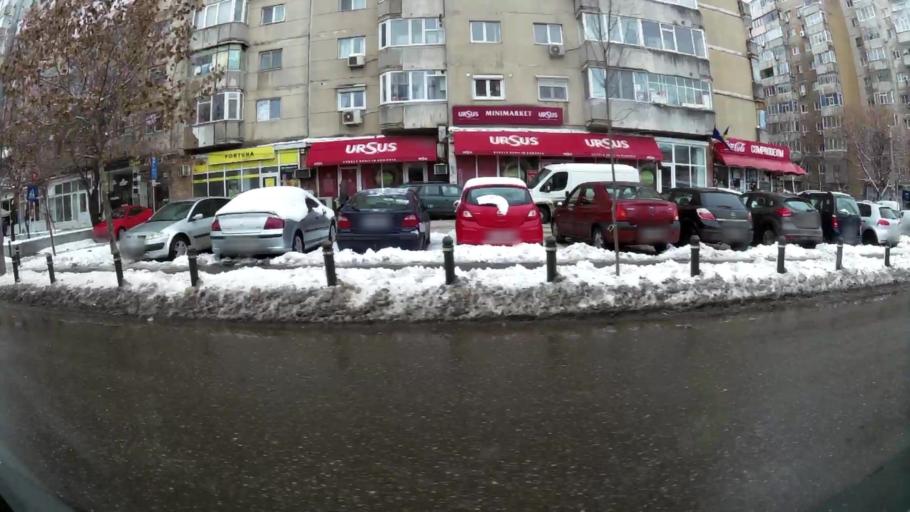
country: RO
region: Bucuresti
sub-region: Municipiul Bucuresti
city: Bucuresti
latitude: 44.3967
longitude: 26.1136
